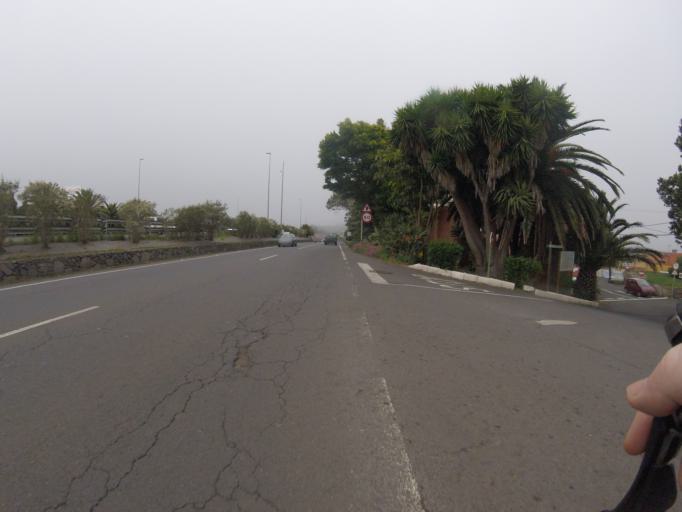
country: ES
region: Canary Islands
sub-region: Provincia de Santa Cruz de Tenerife
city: La Laguna
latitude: 28.4905
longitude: -16.3547
